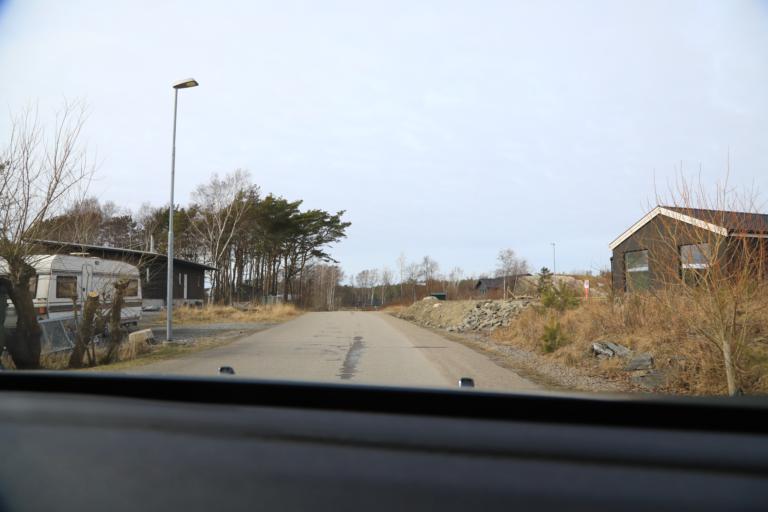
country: SE
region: Halland
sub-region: Kungsbacka Kommun
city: Frillesas
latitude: 57.2301
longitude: 12.1193
